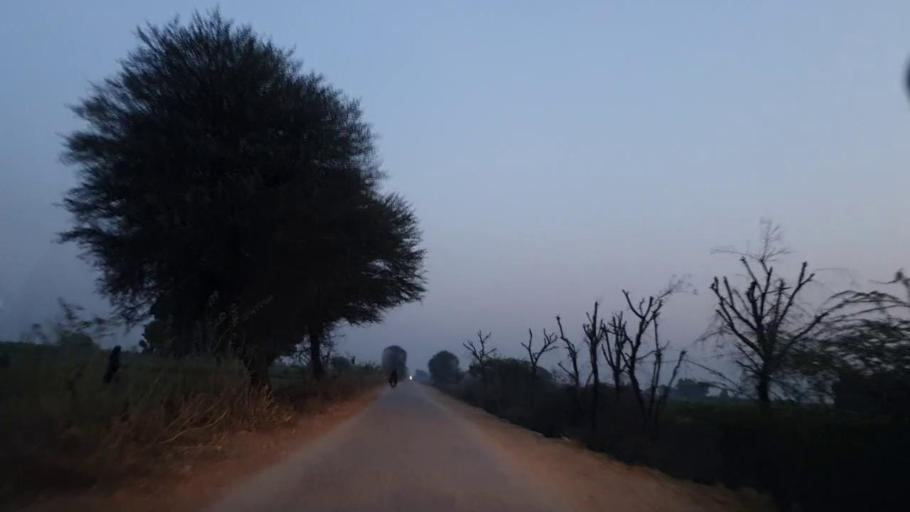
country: PK
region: Sindh
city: Tando Ghulam Ali
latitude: 25.1189
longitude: 68.9016
